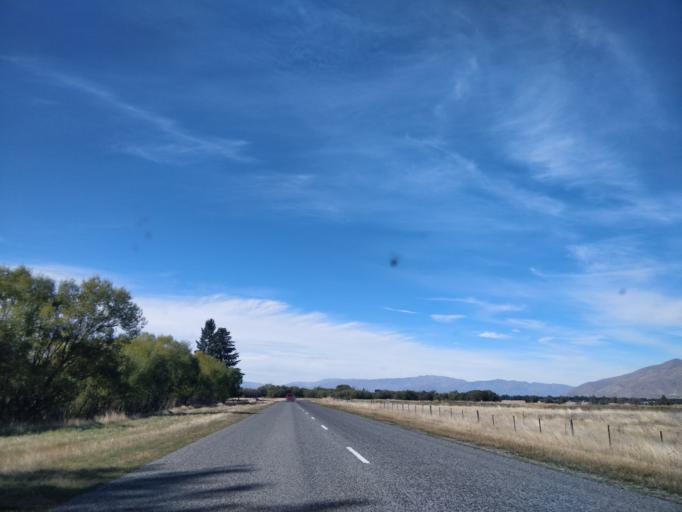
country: NZ
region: Otago
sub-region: Queenstown-Lakes District
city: Wanaka
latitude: -44.2280
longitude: 170.0644
